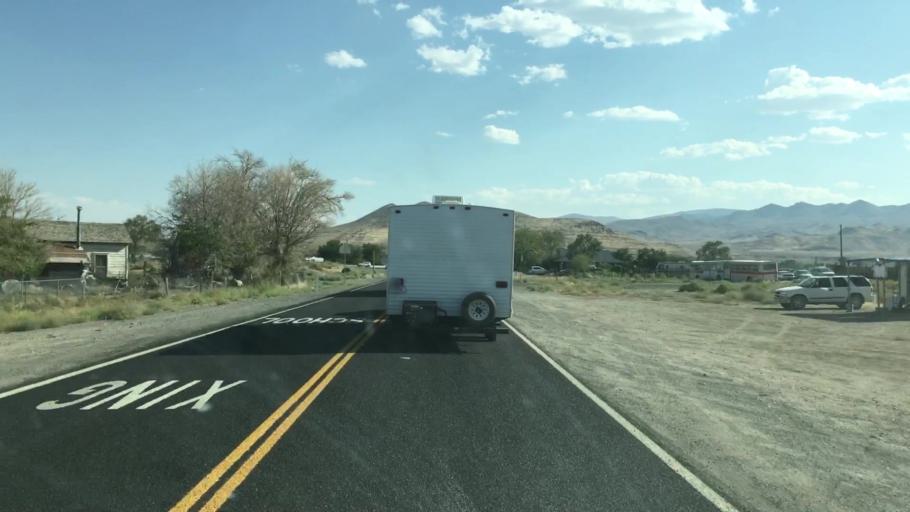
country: US
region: Nevada
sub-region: Lyon County
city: Fernley
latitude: 39.6334
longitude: -119.2906
